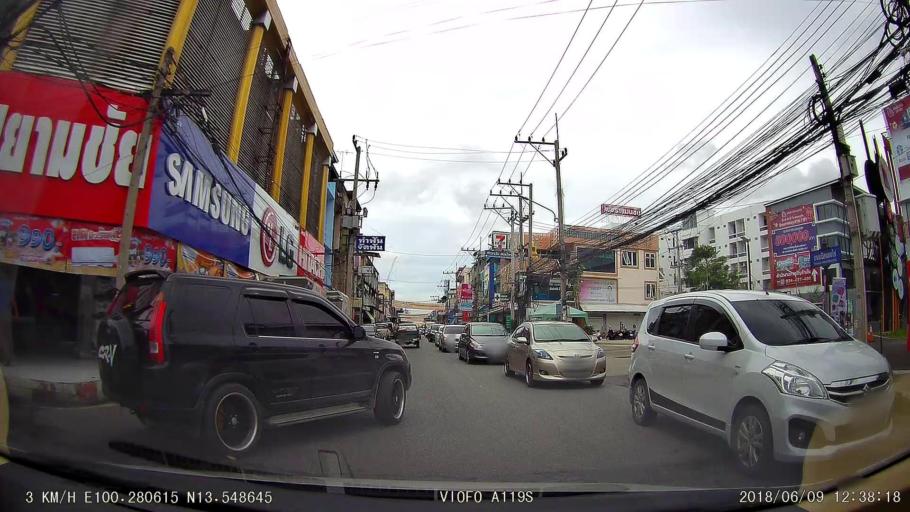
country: TH
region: Samut Sakhon
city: Samut Sakhon
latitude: 13.5484
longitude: 100.2806
